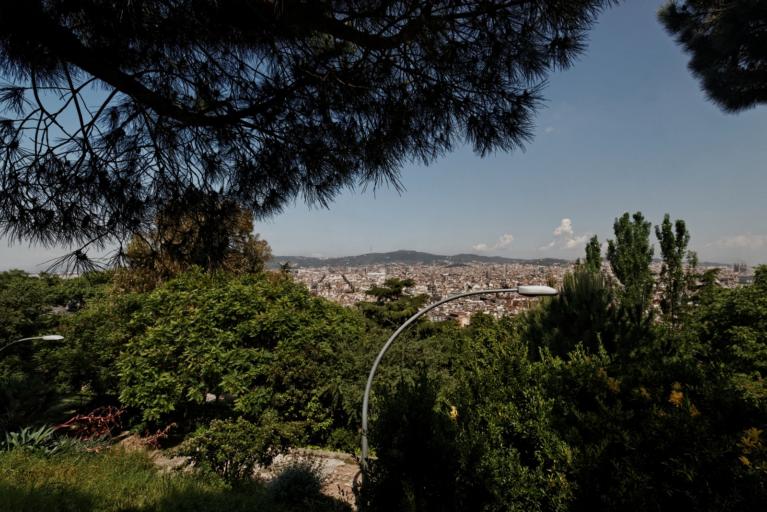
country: ES
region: Catalonia
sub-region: Provincia de Barcelona
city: Sants-Montjuic
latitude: 41.3686
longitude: 2.1664
